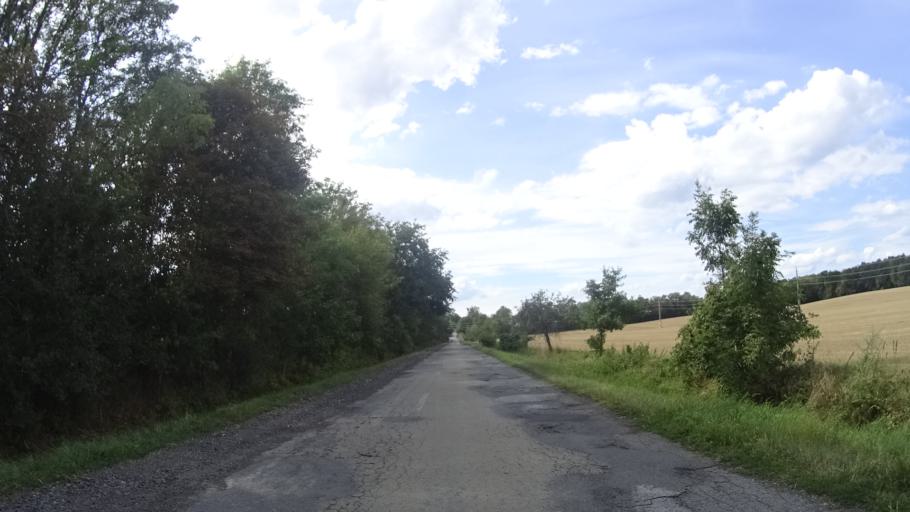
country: CZ
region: Olomoucky
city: Cervenka
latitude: 49.7189
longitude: 17.0382
